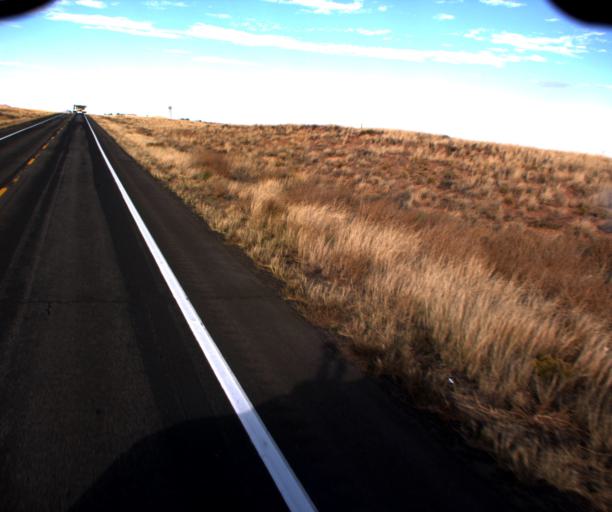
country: US
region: Arizona
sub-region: Apache County
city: Lukachukai
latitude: 36.9603
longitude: -109.3650
